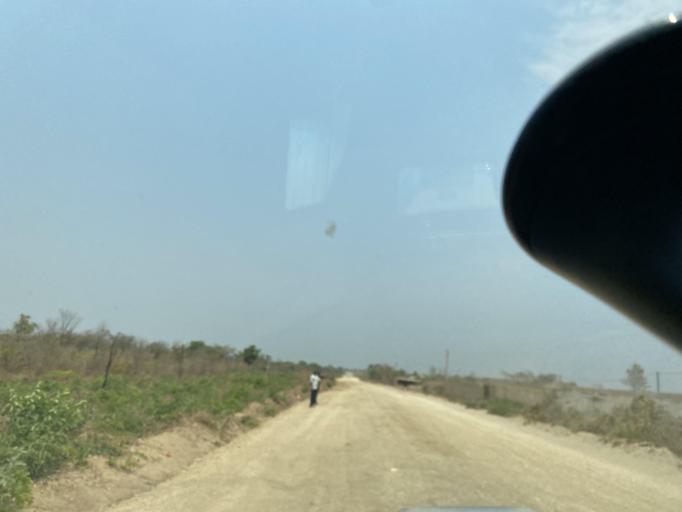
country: ZM
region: Lusaka
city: Lusaka
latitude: -15.5183
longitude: 28.3421
